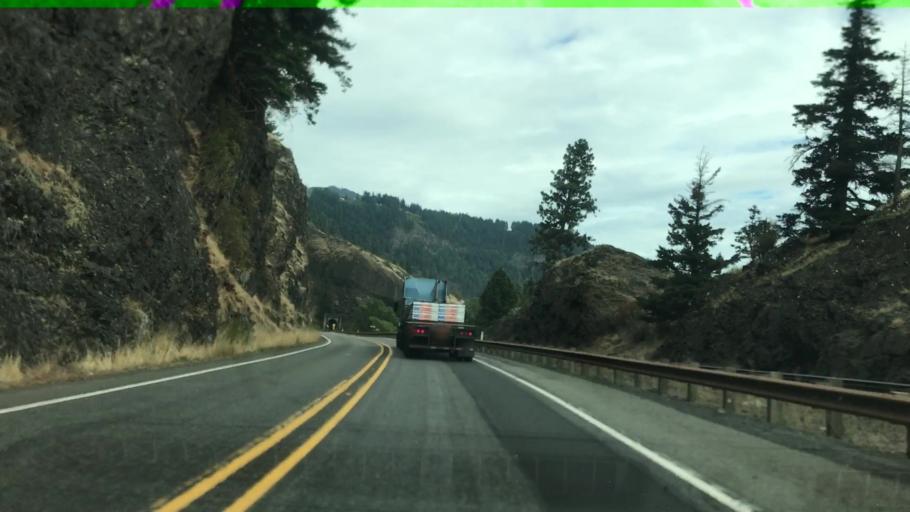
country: US
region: Oregon
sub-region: Hood River County
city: Hood River
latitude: 45.7116
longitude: -121.6234
